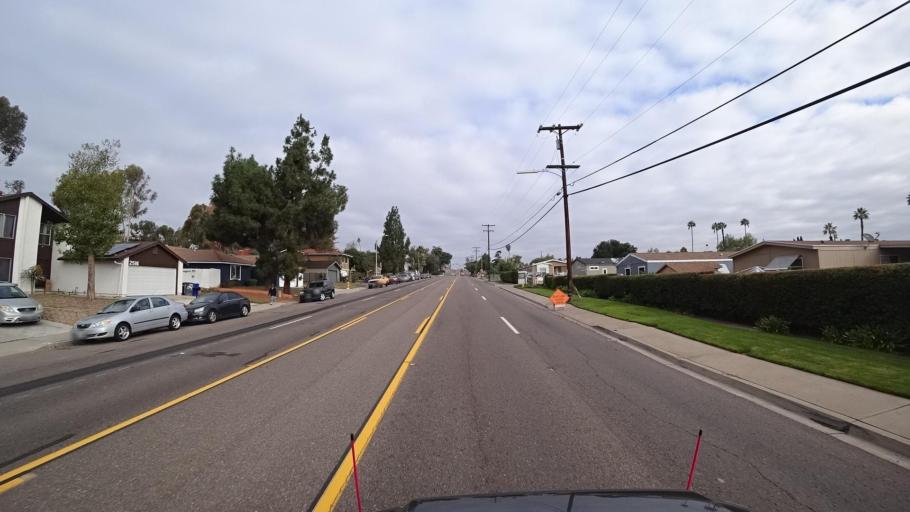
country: US
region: California
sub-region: San Diego County
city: Lemon Grove
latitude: 32.7327
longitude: -117.0145
